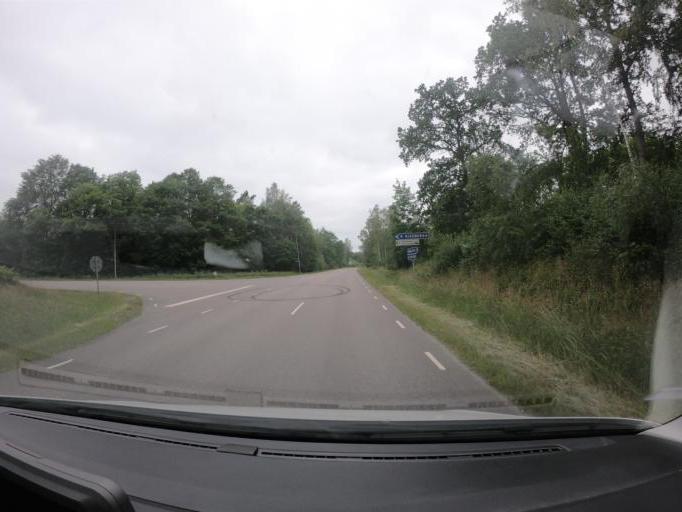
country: SE
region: Skane
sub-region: Perstorps Kommun
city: Perstorp
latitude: 56.1232
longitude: 13.4034
